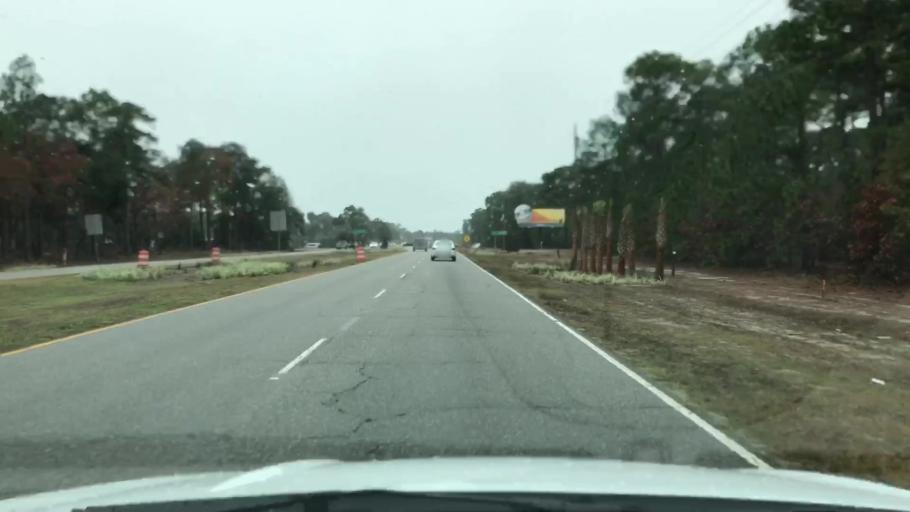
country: US
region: South Carolina
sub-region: Horry County
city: Myrtle Beach
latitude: 33.7490
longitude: -78.8341
